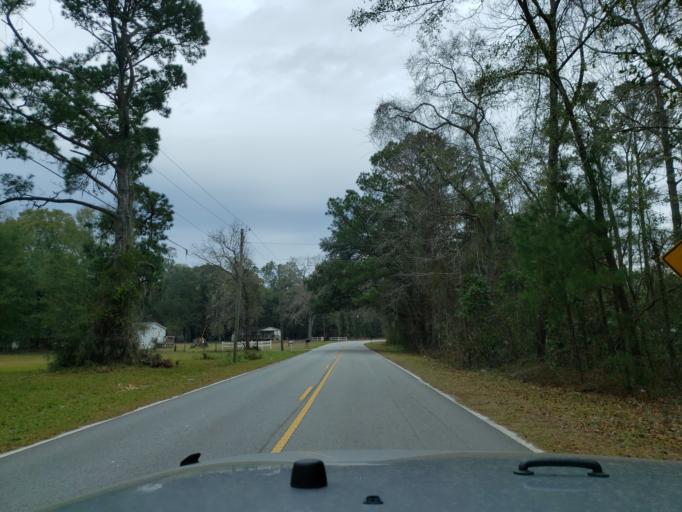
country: US
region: Georgia
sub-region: Chatham County
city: Georgetown
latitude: 32.0368
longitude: -81.1876
